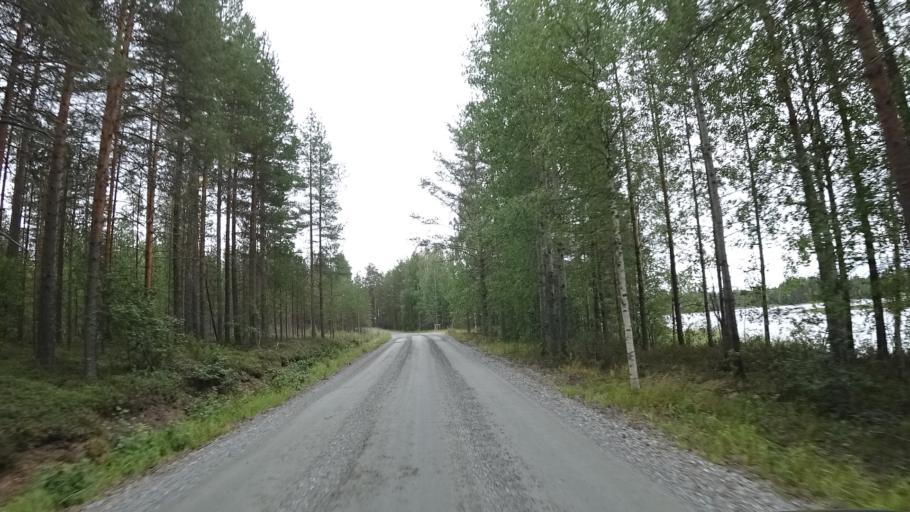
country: FI
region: North Karelia
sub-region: Pielisen Karjala
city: Lieksa
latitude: 63.3812
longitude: 30.3423
